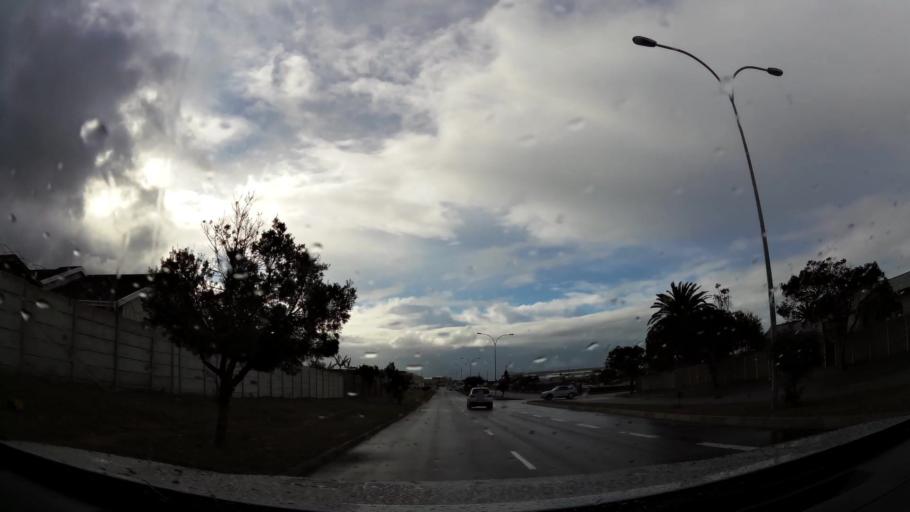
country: ZA
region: Western Cape
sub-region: Eden District Municipality
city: Mossel Bay
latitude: -34.1865
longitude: 22.1141
